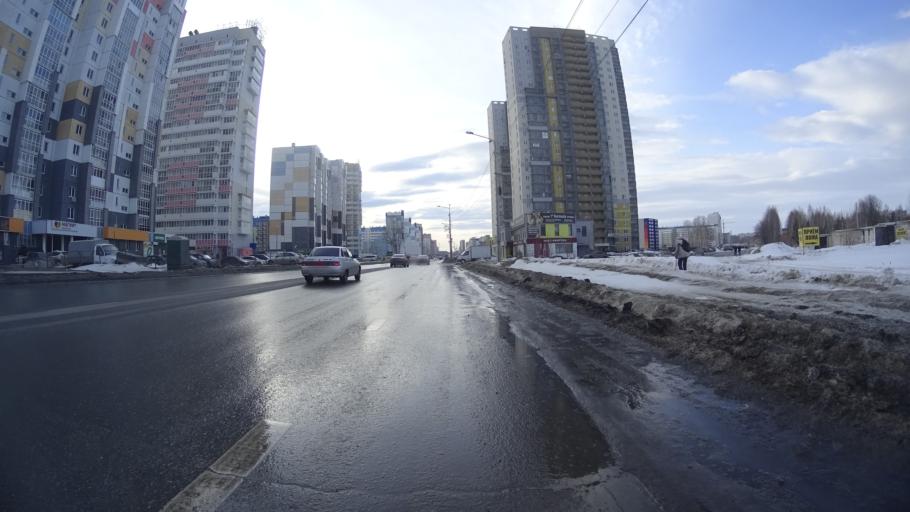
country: RU
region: Chelyabinsk
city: Roshchino
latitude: 55.2087
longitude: 61.3044
